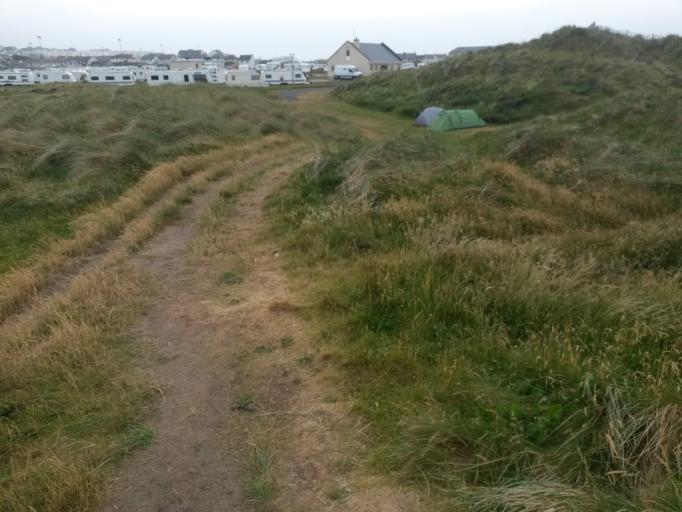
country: IE
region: Connaught
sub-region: Sligo
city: Strandhill
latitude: 54.2737
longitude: -8.6063
